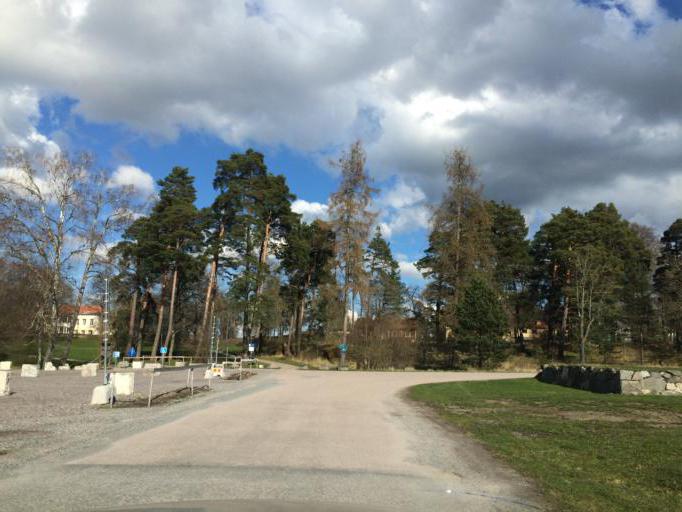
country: SE
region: Soedermanland
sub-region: Eskilstuna Kommun
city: Eskilstuna
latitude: 59.4458
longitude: 16.6203
